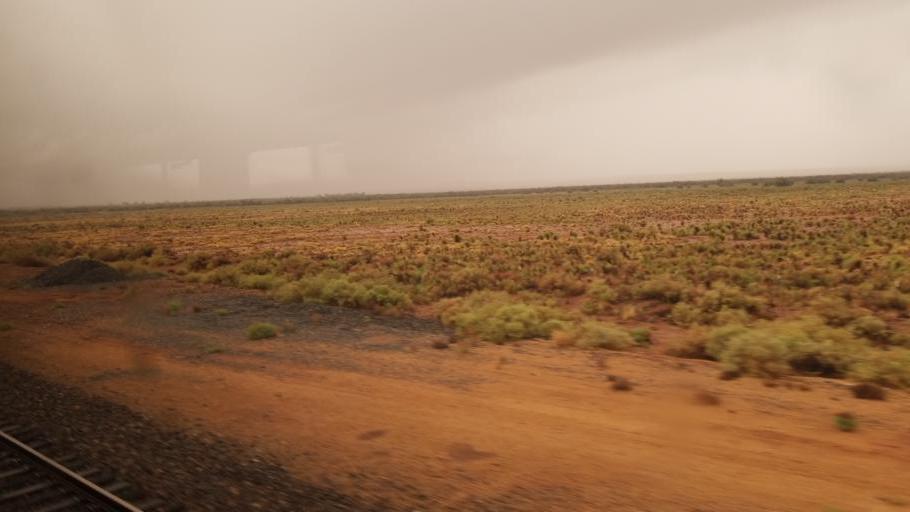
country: US
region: Arizona
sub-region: Navajo County
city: Joseph City
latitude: 34.9675
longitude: -110.4879
